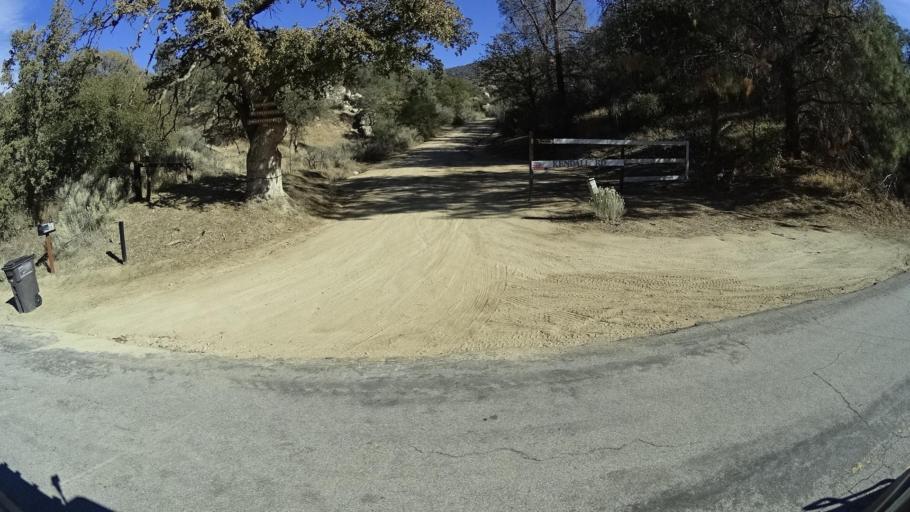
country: US
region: California
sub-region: Kern County
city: Bodfish
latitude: 35.4713
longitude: -118.5312
